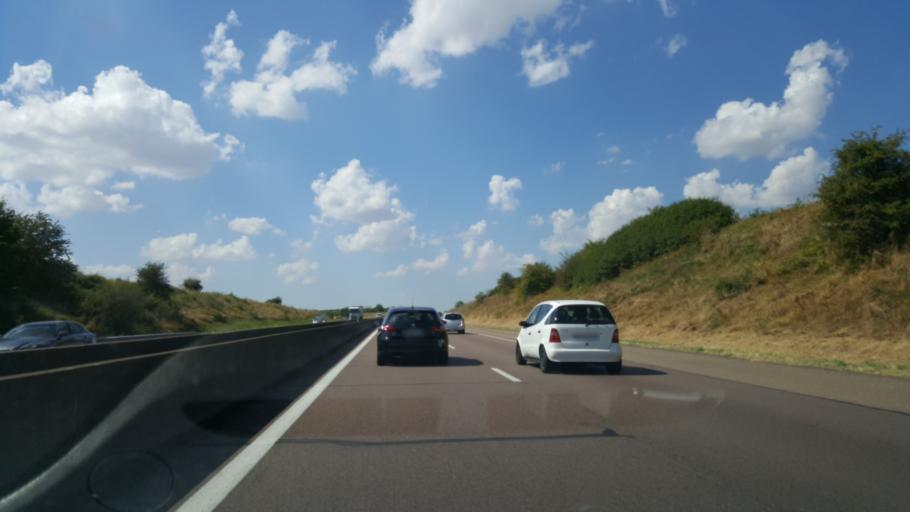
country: FR
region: Bourgogne
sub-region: Departement de la Cote-d'Or
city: Semur-en-Auxois
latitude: 47.4385
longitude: 4.3022
